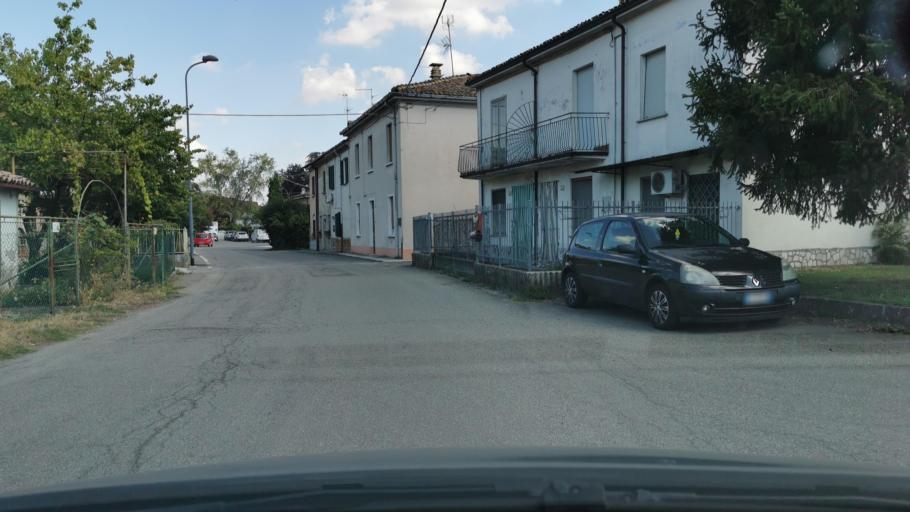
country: IT
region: Emilia-Romagna
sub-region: Provincia di Piacenza
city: Caorso
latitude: 45.0379
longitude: 9.8533
